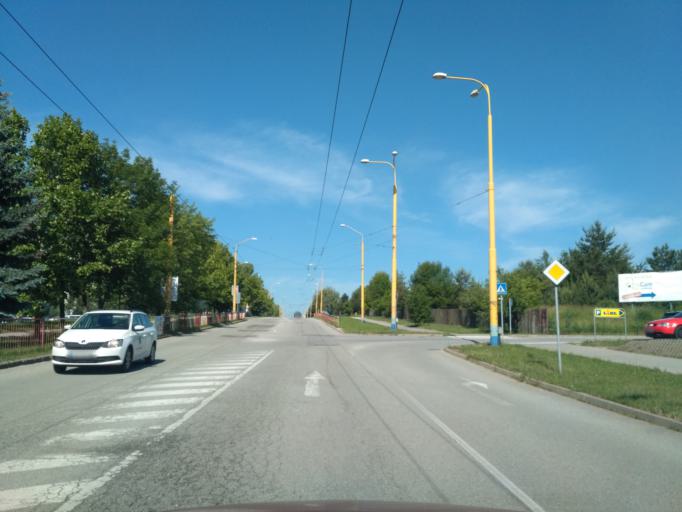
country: SK
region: Kosicky
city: Kosice
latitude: 48.7192
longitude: 21.2125
